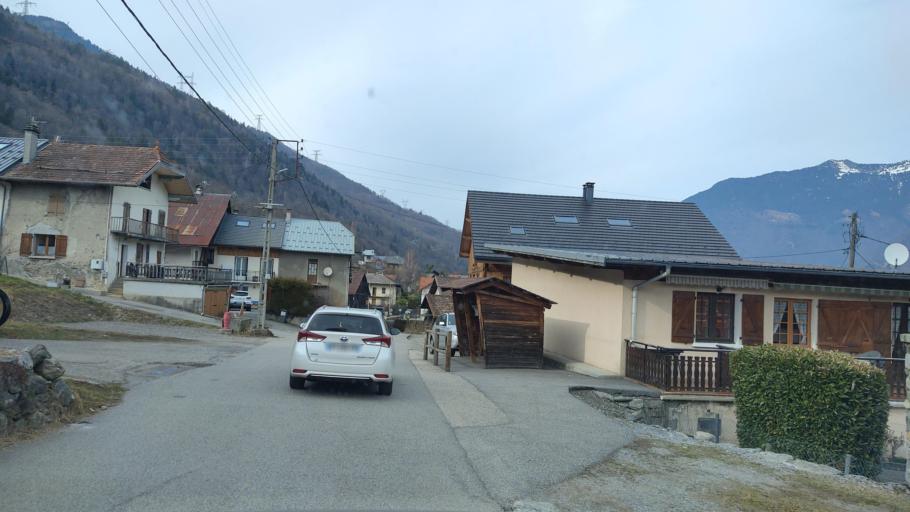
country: FR
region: Rhone-Alpes
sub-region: Departement de la Savoie
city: La Bathie
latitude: 45.6128
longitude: 6.4361
